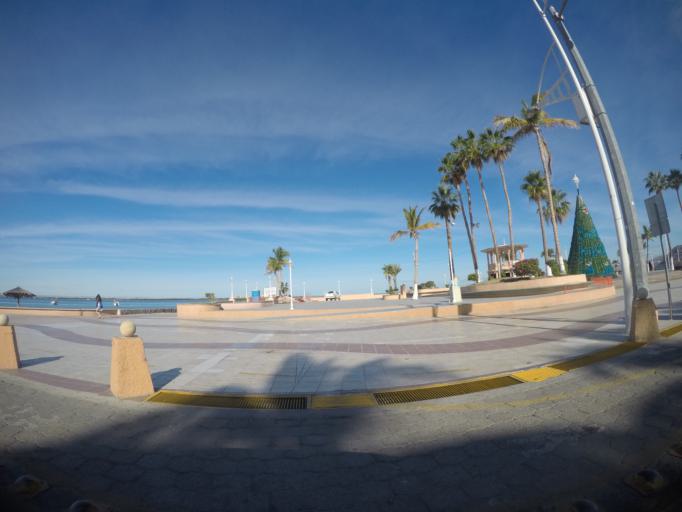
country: MX
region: Baja California Sur
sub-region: La Paz
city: La Paz
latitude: 24.1929
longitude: -110.2955
